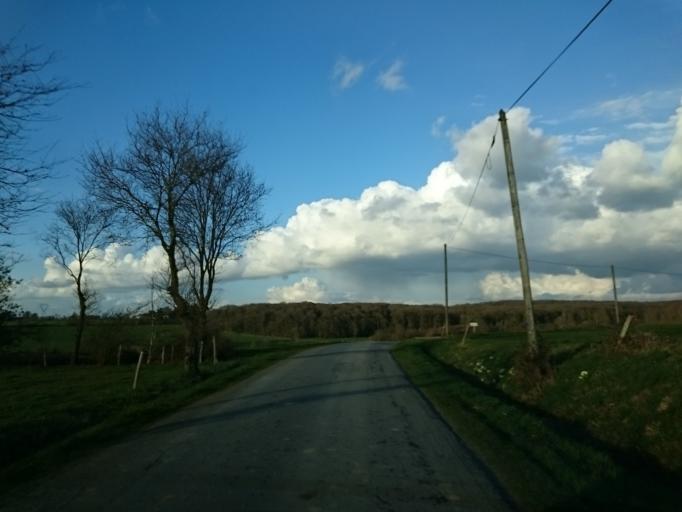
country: FR
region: Brittany
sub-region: Departement d'Ille-et-Vilaine
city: Pance
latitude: 47.9105
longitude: -1.6391
